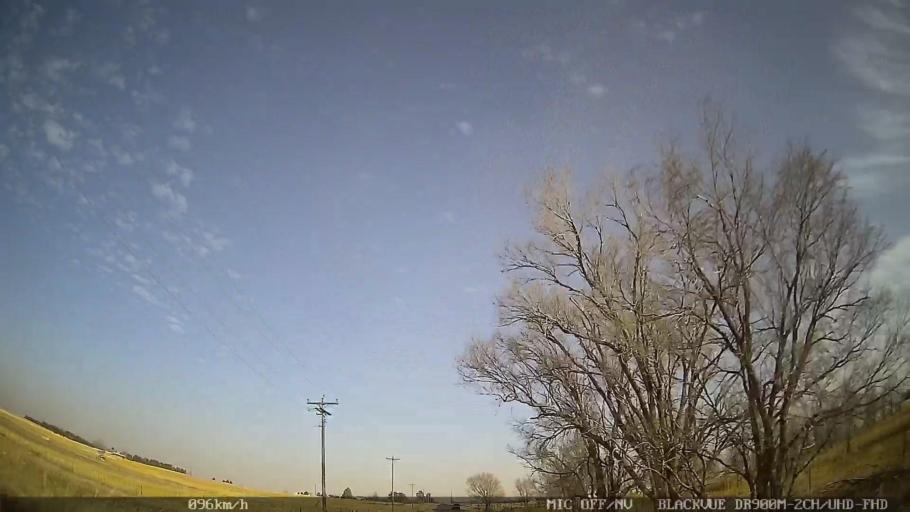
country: US
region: New Mexico
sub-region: Curry County
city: Texico
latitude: 34.4193
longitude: -103.1250
